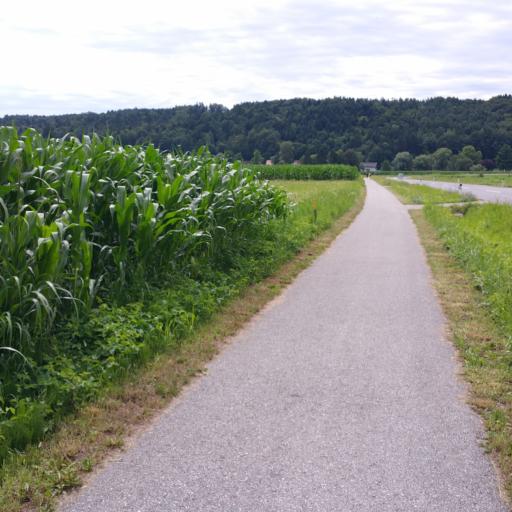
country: AT
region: Styria
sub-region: Politischer Bezirk Leibnitz
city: Gleinstatten
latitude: 46.7515
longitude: 15.3715
